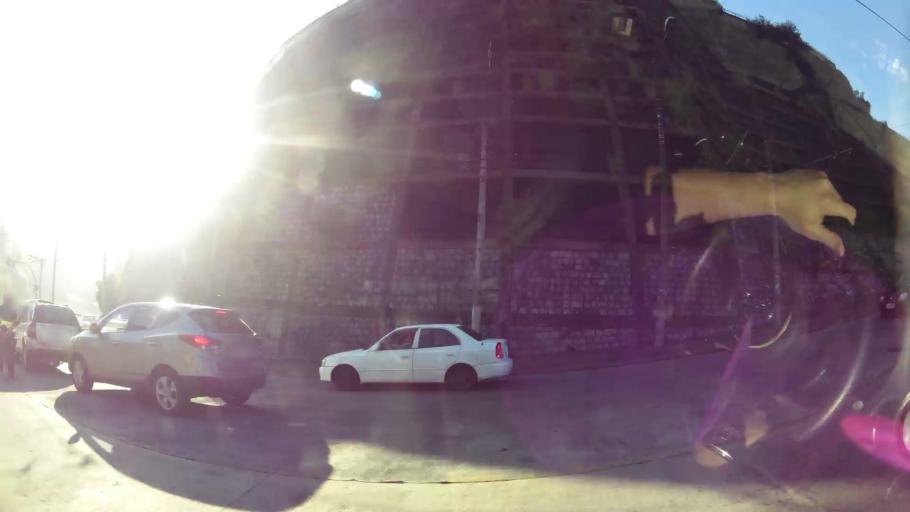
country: EC
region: Pichincha
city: Quito
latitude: -0.2339
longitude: -78.5143
